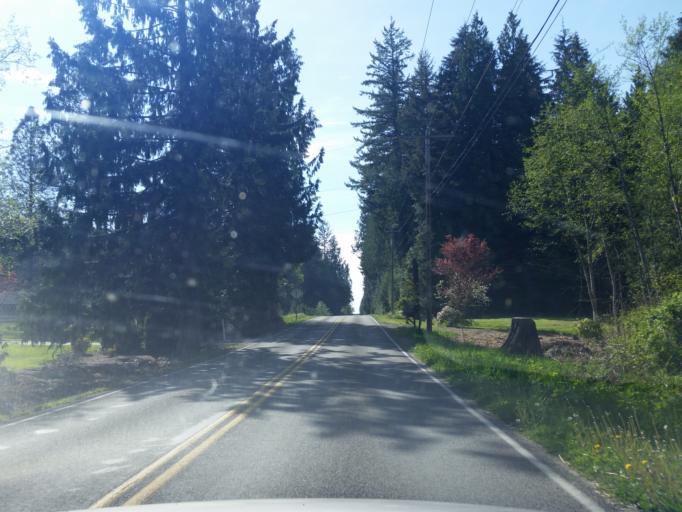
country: US
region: Washington
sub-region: Snohomish County
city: Three Lakes
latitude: 47.9633
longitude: -122.0020
